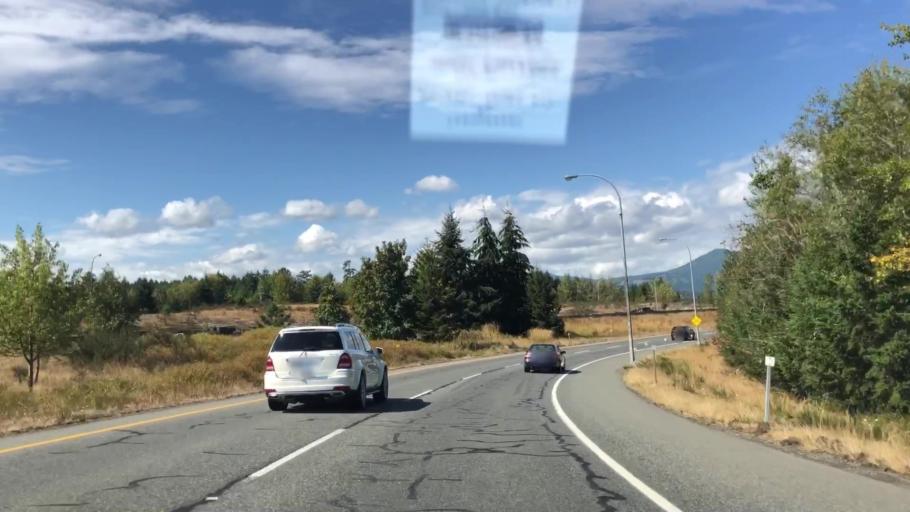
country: CA
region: British Columbia
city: Nanaimo
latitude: 49.1108
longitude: -123.9009
